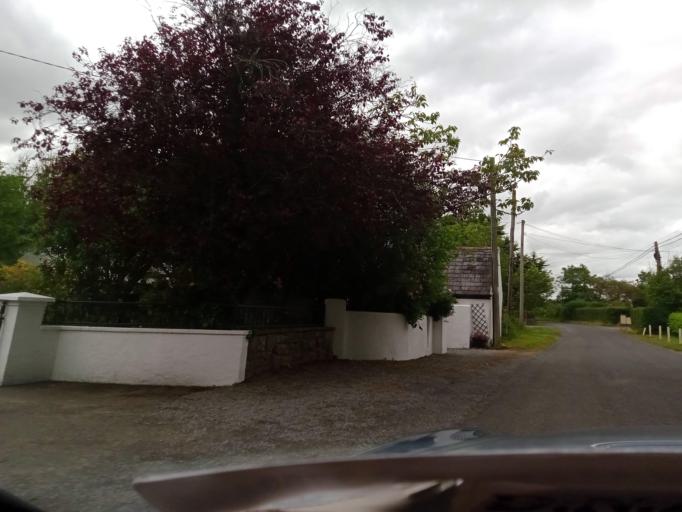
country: IE
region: Leinster
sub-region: Kilkenny
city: Thomastown
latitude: 52.5720
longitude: -7.1948
